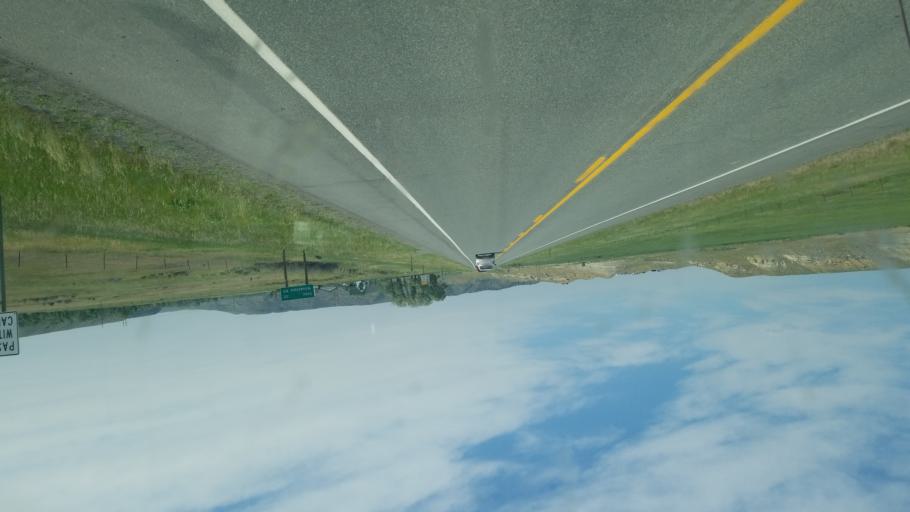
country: US
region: Wyoming
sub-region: Park County
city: Cody
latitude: 44.1630
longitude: -108.8761
